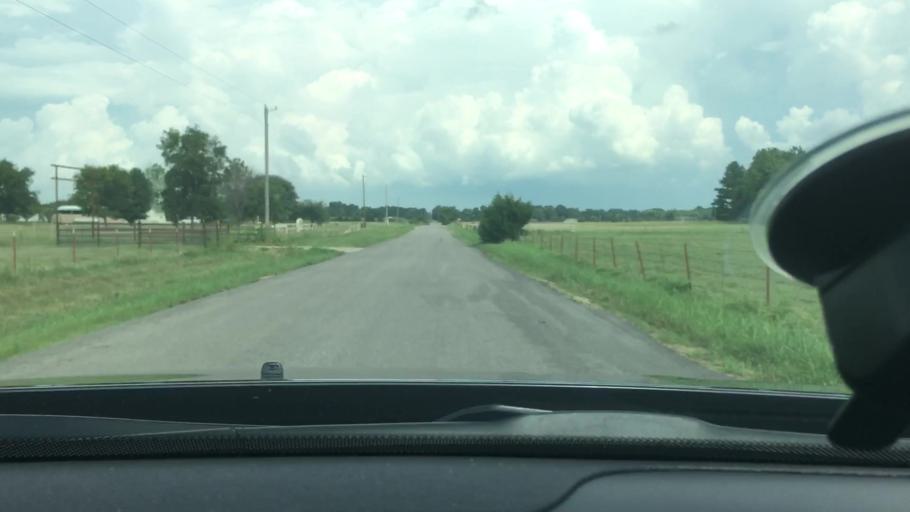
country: US
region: Oklahoma
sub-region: Carter County
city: Dickson
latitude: 34.1932
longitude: -96.8982
